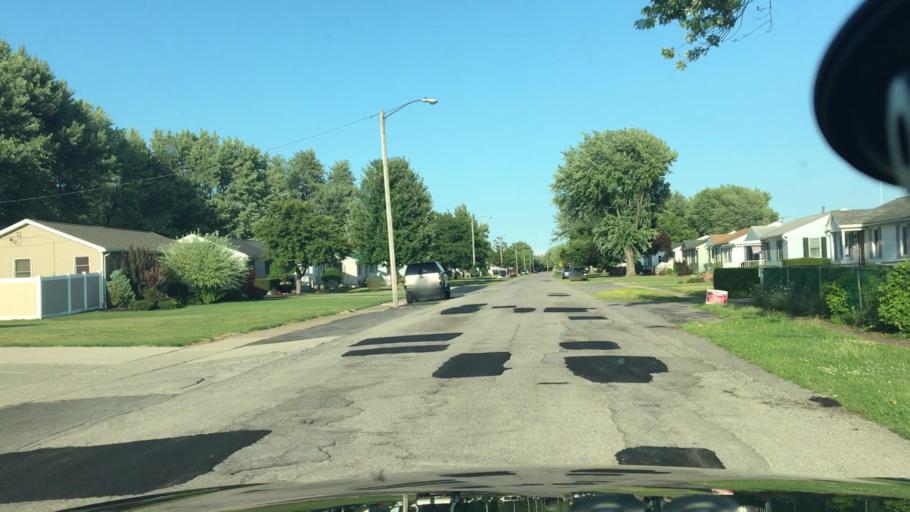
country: US
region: New York
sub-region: Erie County
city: Blasdell
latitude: 42.8005
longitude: -78.8231
